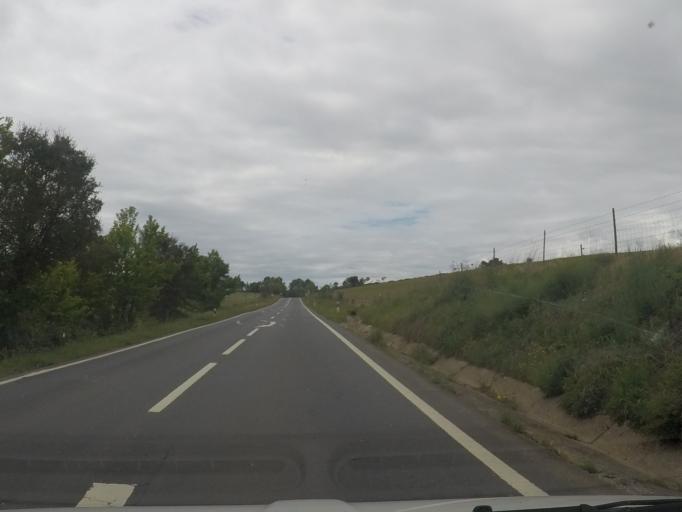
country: PT
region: Setubal
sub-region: Santiago do Cacem
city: Cercal
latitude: 37.8247
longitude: -8.6934
